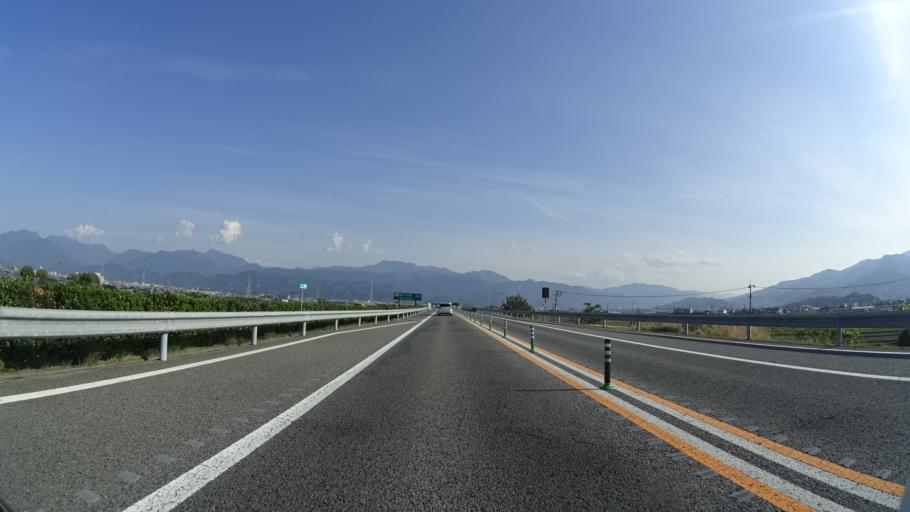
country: JP
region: Ehime
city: Saijo
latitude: 33.9388
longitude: 133.0693
